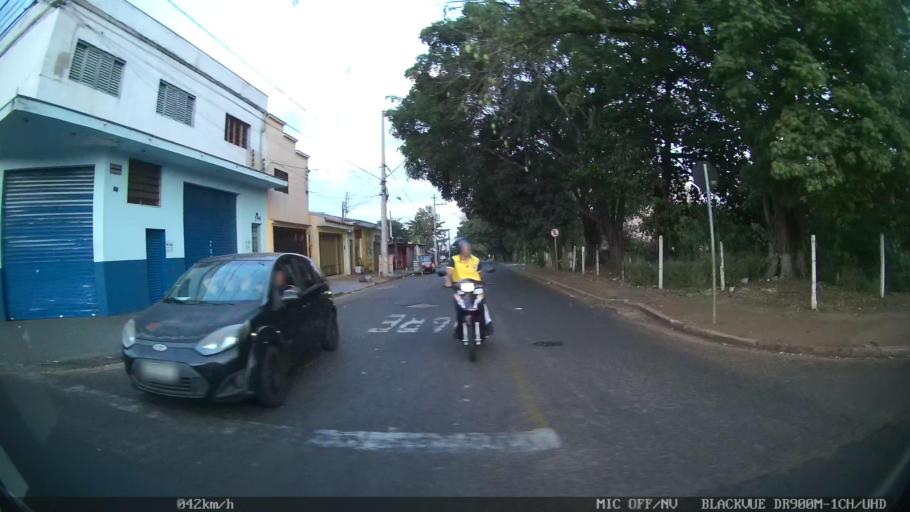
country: BR
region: Sao Paulo
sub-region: Ribeirao Preto
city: Ribeirao Preto
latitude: -21.1488
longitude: -47.8220
